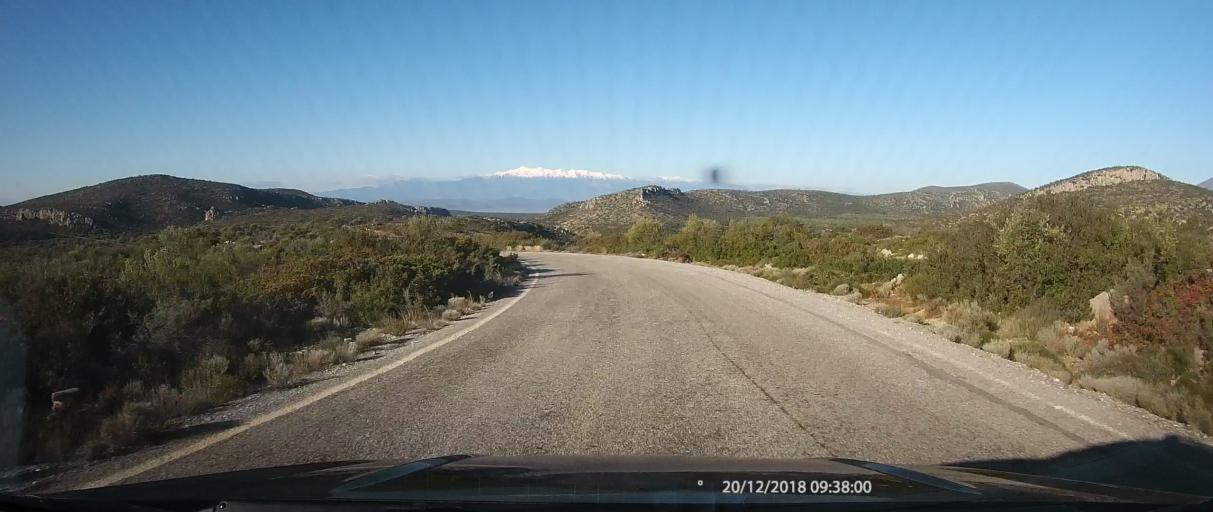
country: GR
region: Peloponnese
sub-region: Nomos Lakonias
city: Kato Glikovrisi
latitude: 36.9399
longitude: 22.7978
